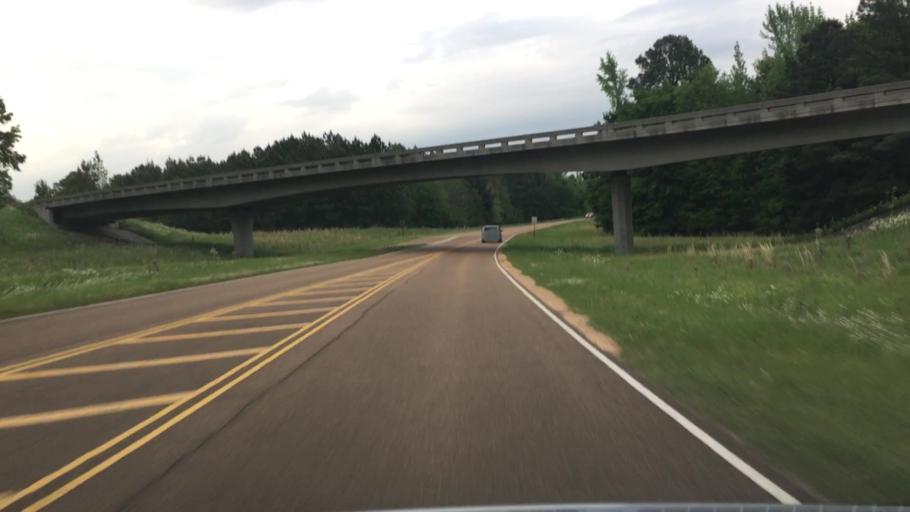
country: US
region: Mississippi
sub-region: Hinds County
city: Clinton
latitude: 32.3847
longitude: -90.2580
